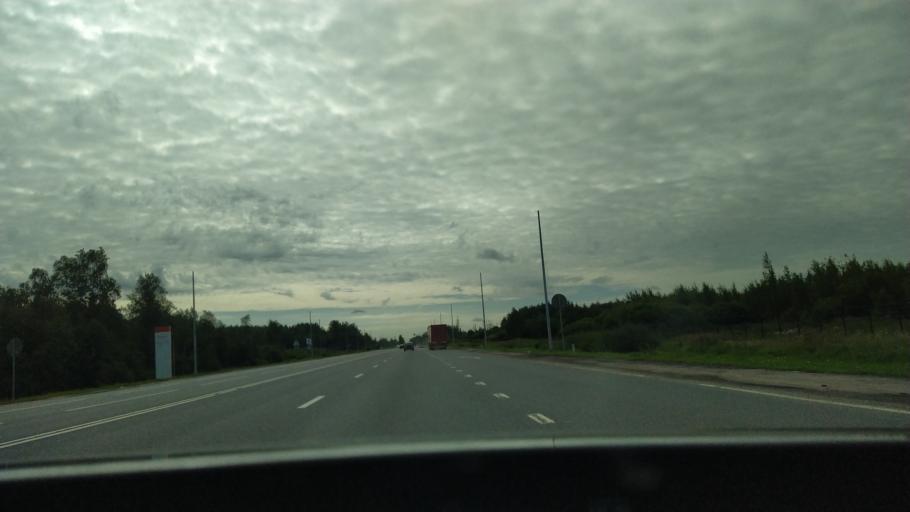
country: RU
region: Leningrad
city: Tosno
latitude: 59.5712
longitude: 30.8218
